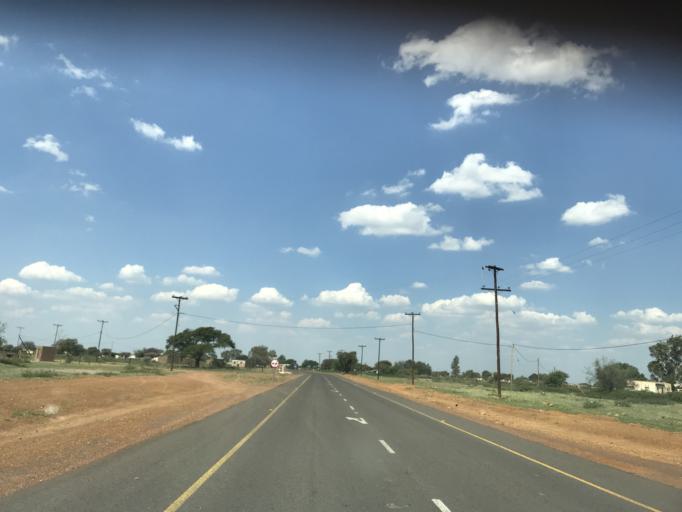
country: BW
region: South East
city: Janeng
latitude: -25.5626
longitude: 25.5905
